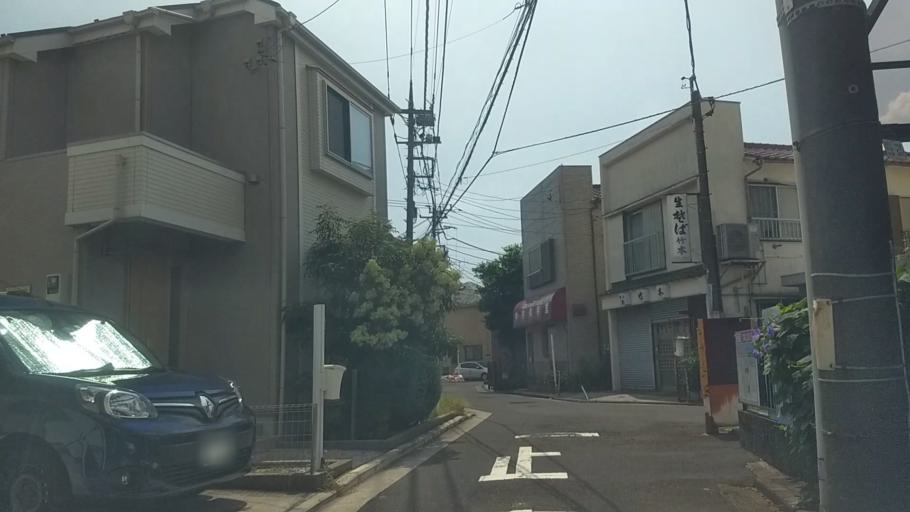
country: JP
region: Kanagawa
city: Yokohama
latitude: 35.5114
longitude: 139.6496
